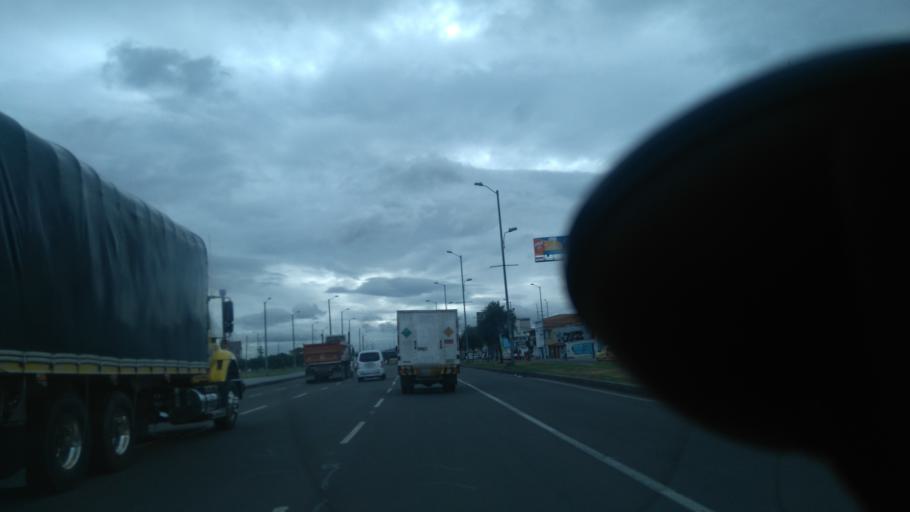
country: CO
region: Bogota D.C.
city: Bogota
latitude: 4.6301
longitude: -74.1314
